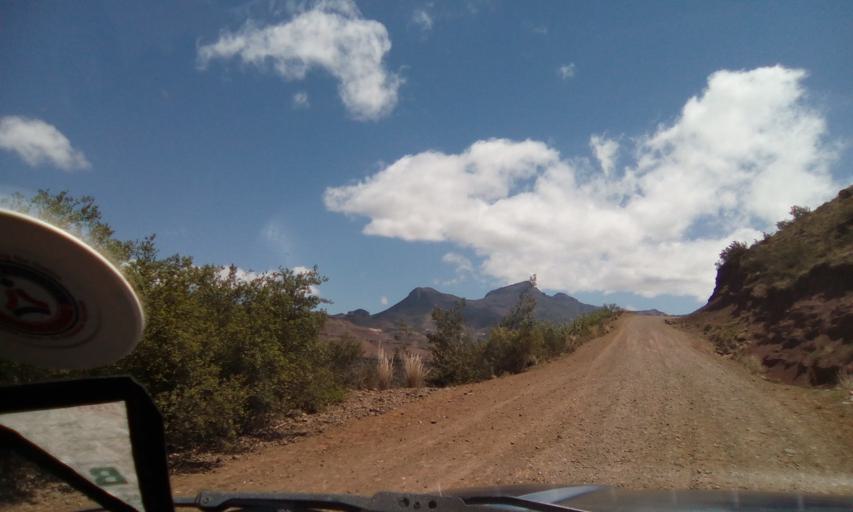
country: LS
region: Qacha's Nek
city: Qacha's Nek
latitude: -30.0655
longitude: 28.6239
